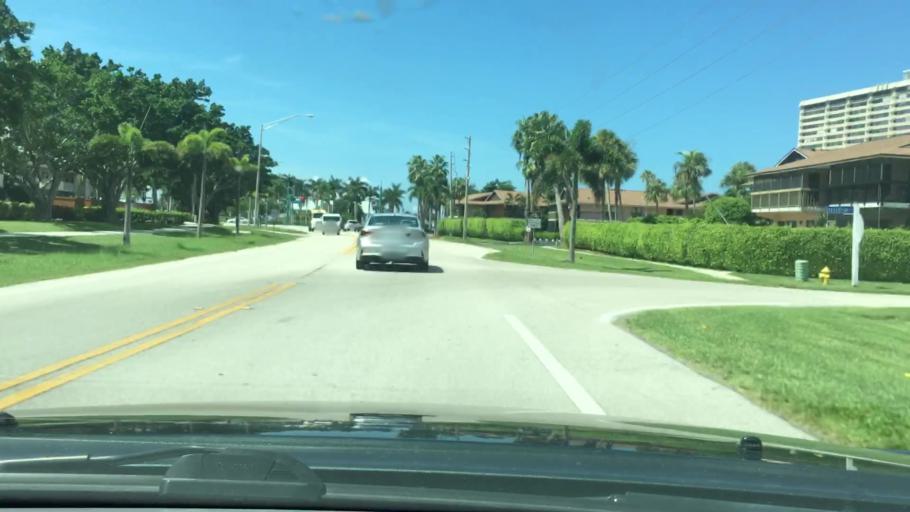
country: US
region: Florida
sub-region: Collier County
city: Marco
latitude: 25.9369
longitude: -81.7299
